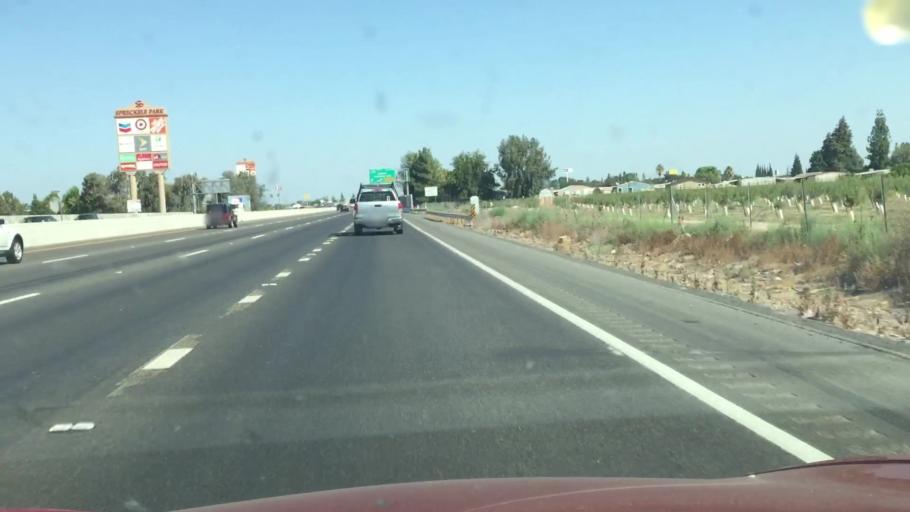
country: US
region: California
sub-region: San Joaquin County
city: Manteca
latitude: 37.7920
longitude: -121.1897
